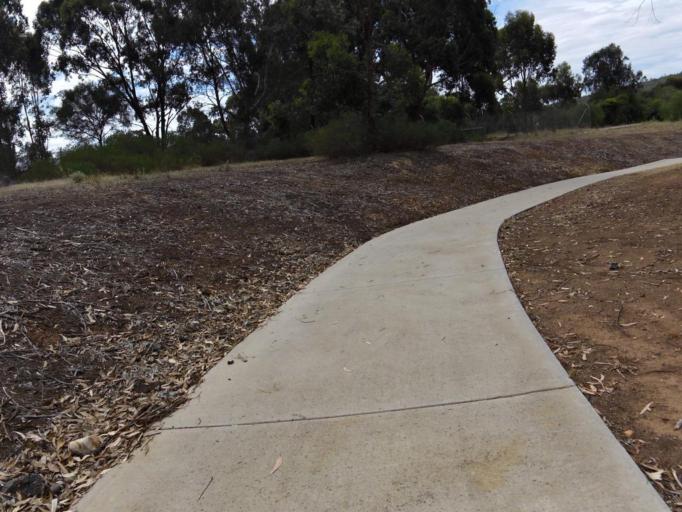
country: AU
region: Victoria
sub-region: Greater Bendigo
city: Kennington
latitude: -36.9250
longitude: 144.7084
